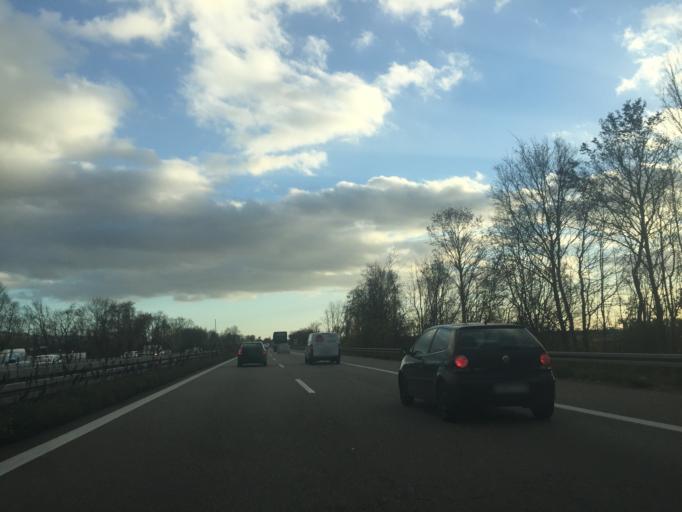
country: DE
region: Baden-Wuerttemberg
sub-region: Karlsruhe Region
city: Schriesheim
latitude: 49.4638
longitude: 8.6450
